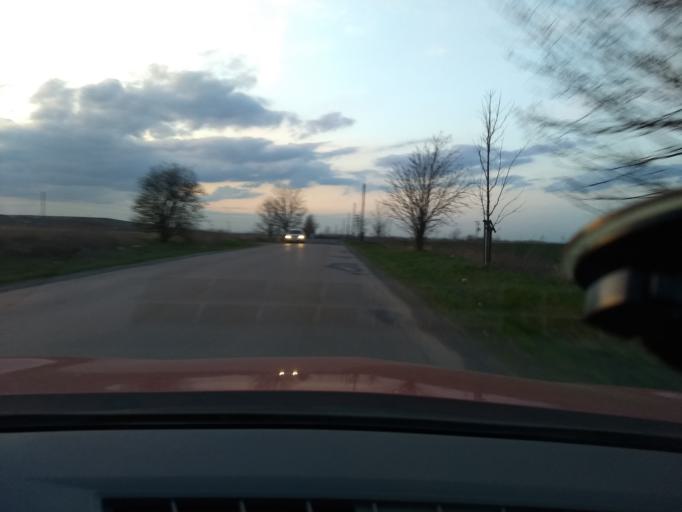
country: CZ
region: Central Bohemia
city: Rudna
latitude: 50.0501
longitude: 14.2549
